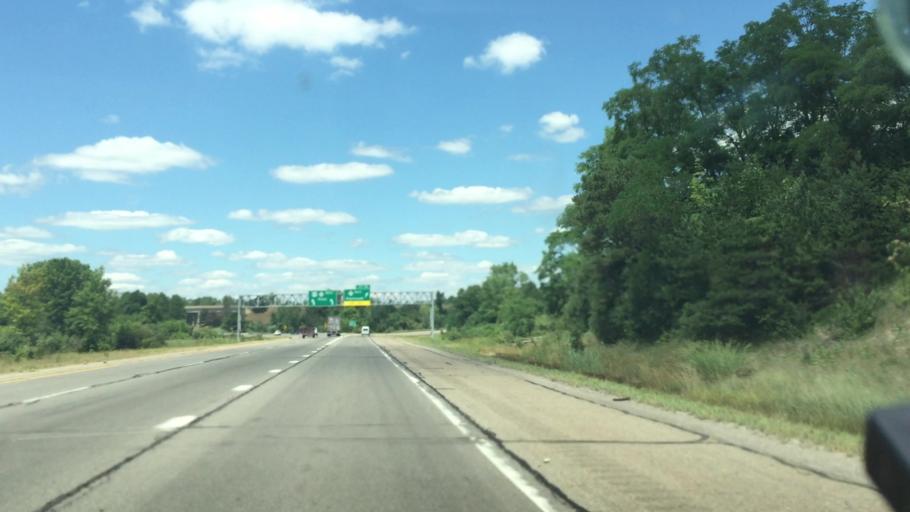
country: US
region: Michigan
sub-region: Washtenaw County
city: Ann Arbor
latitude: 42.3184
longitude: -83.6883
